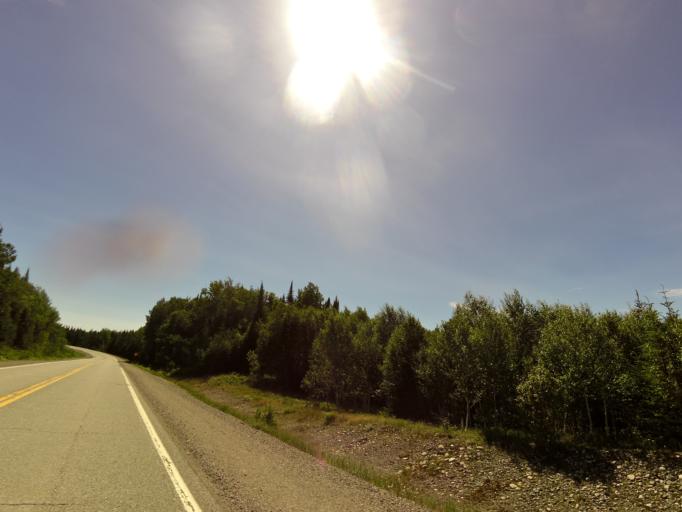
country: CA
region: Quebec
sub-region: Nord-du-Quebec
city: Lebel-sur-Quevillon
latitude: 48.8201
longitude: -77.1251
